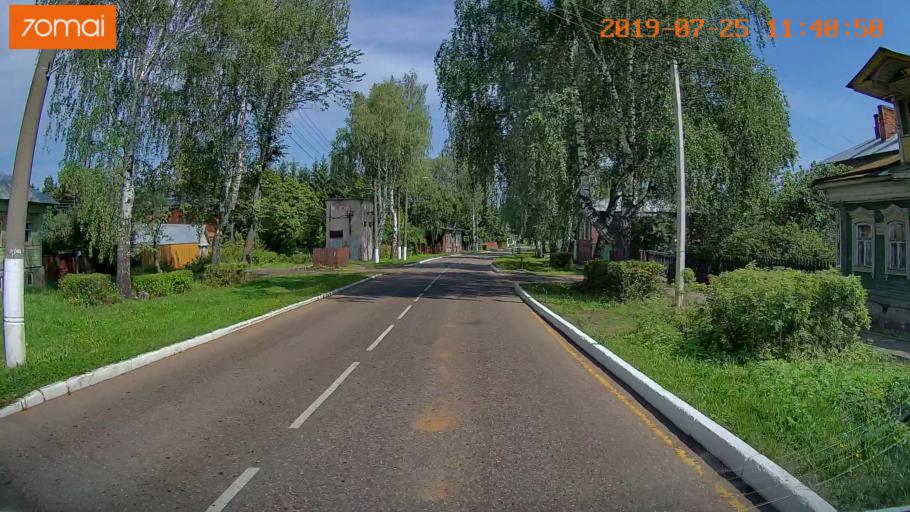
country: RU
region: Ivanovo
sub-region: Privolzhskiy Rayon
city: Ples
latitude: 57.4550
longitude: 41.5097
